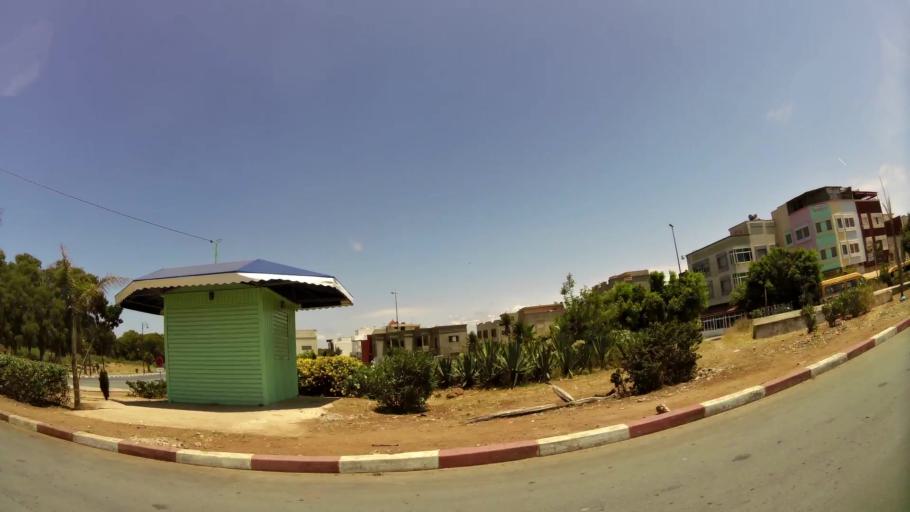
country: MA
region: Gharb-Chrarda-Beni Hssen
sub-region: Kenitra Province
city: Kenitra
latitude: 34.2665
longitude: -6.6445
